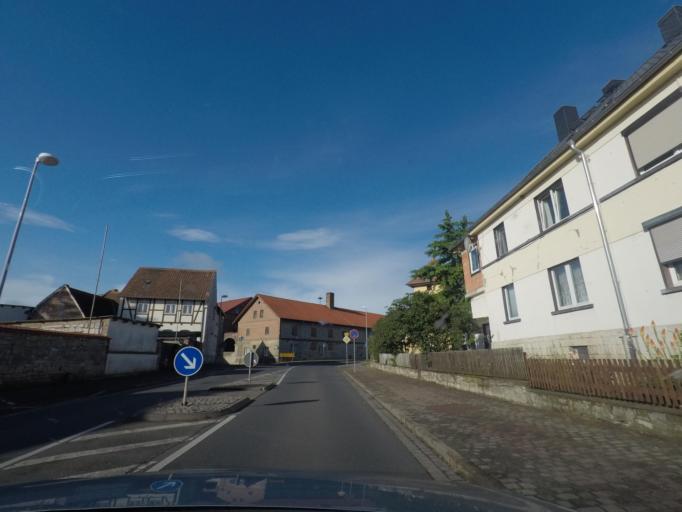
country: DE
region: Saxony-Anhalt
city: Huy-Neinstedt
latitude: 51.9864
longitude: 10.8887
